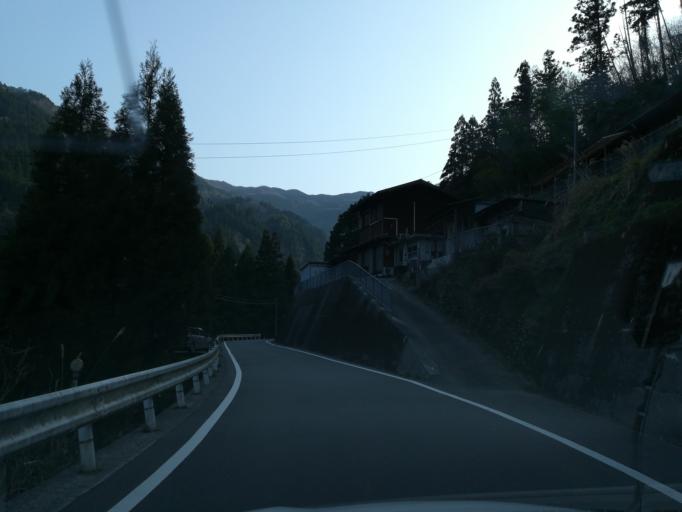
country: JP
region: Tokushima
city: Ikedacho
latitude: 33.8811
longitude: 133.8411
